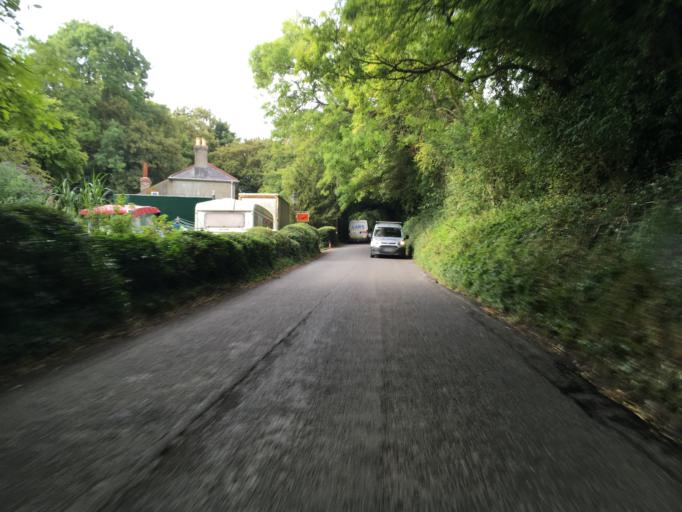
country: GB
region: England
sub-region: Hampshire
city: Colden Common
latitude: 51.0009
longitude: -1.2717
